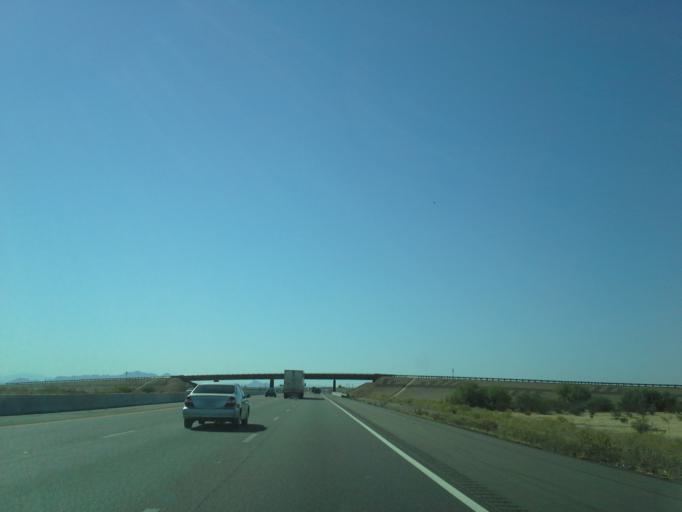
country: US
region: Arizona
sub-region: Pinal County
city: Casa Grande
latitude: 32.9402
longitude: -111.7028
